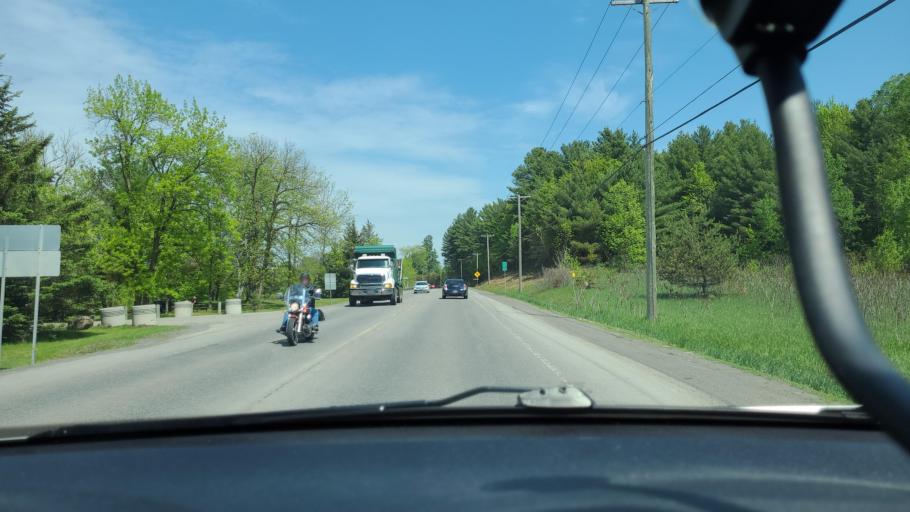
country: CA
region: Quebec
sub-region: Laurentides
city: Lachute
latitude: 45.6648
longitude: -74.2935
